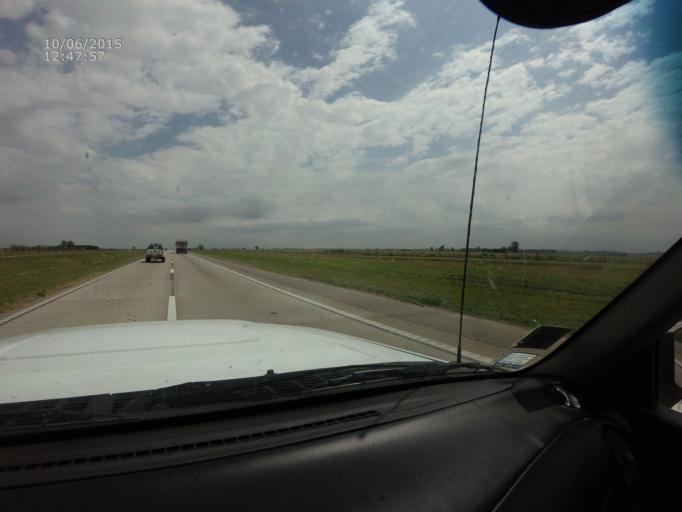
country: AR
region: Santa Fe
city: Canada de Gomez
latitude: -32.8395
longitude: -61.4391
